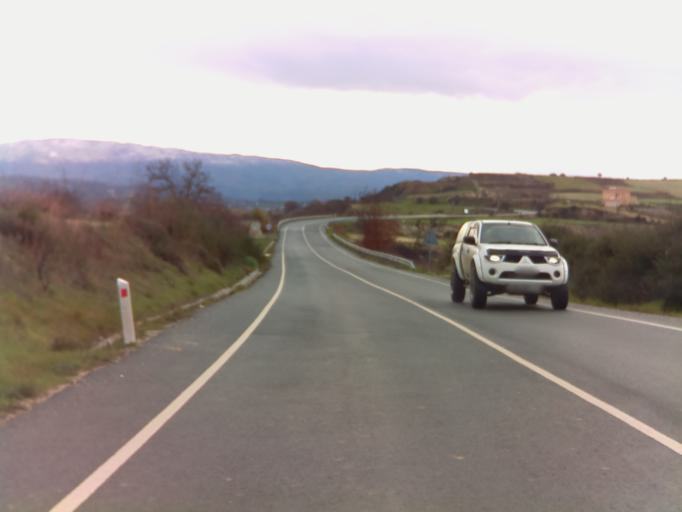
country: CY
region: Pafos
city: Tala
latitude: 34.8972
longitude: 32.4557
